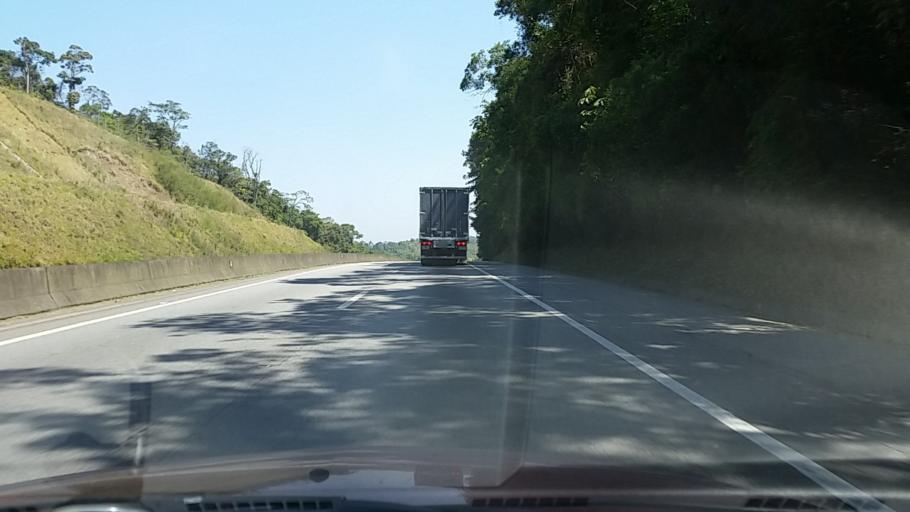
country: BR
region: Sao Paulo
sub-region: Juquitiba
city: Juquitiba
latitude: -23.9643
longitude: -47.1255
